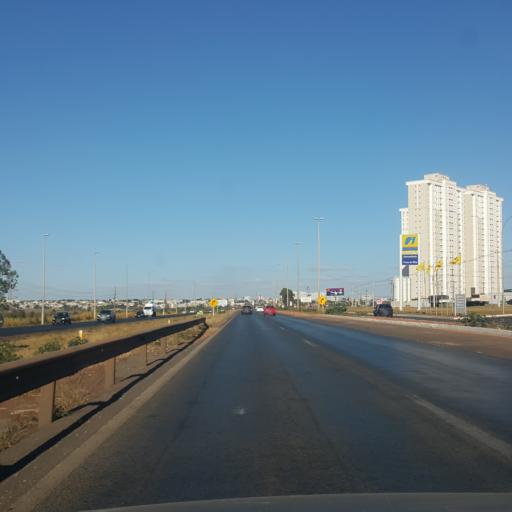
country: BR
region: Federal District
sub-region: Brasilia
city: Brasilia
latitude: -15.7949
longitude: -48.0960
